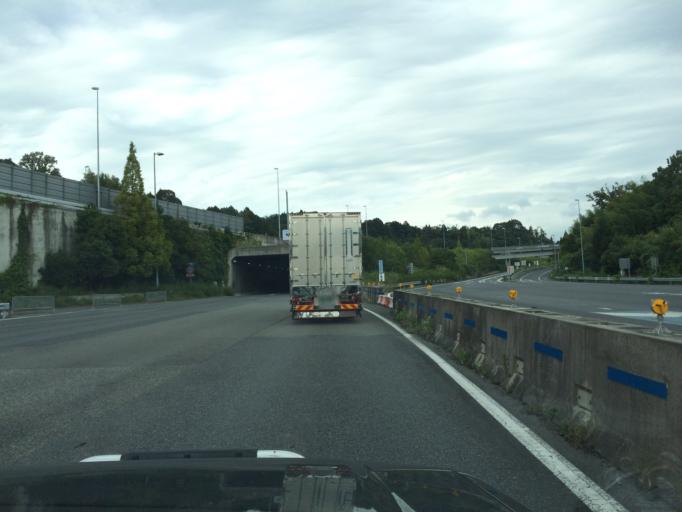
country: JP
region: Mie
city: Kameyama
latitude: 34.8613
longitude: 136.4130
